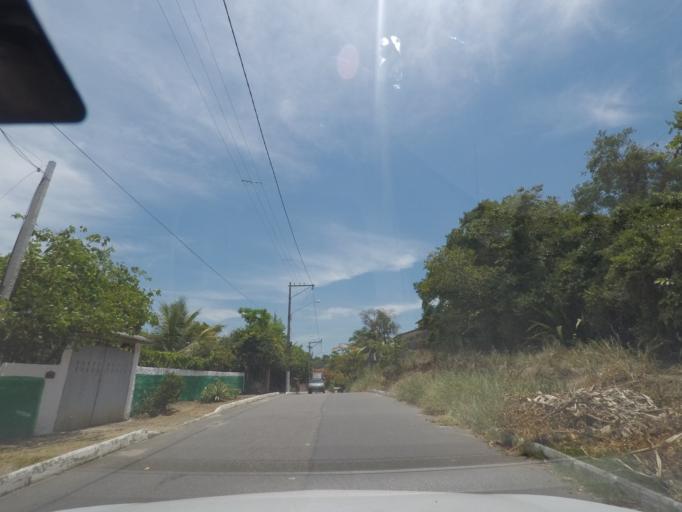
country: BR
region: Rio de Janeiro
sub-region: Marica
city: Marica
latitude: -22.9294
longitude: -42.8244
